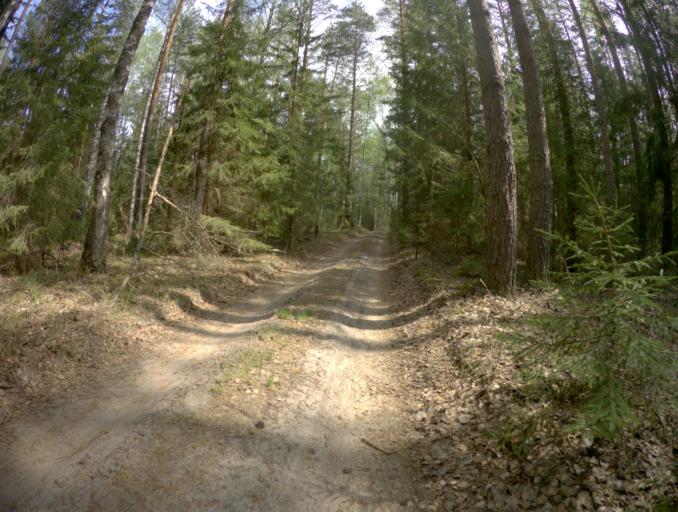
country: RU
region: Ivanovo
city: Yuzha
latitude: 56.4807
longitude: 42.1399
